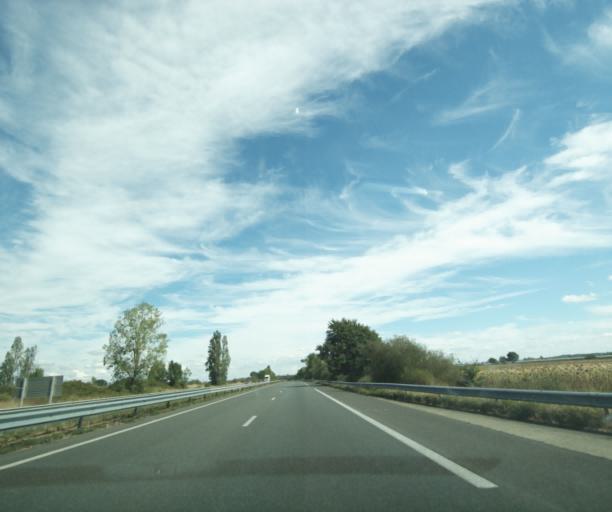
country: FR
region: Midi-Pyrenees
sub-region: Departement du Tarn-et-Garonne
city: Saint-Nicolas-de-la-Grave
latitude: 44.0406
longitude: 1.0212
